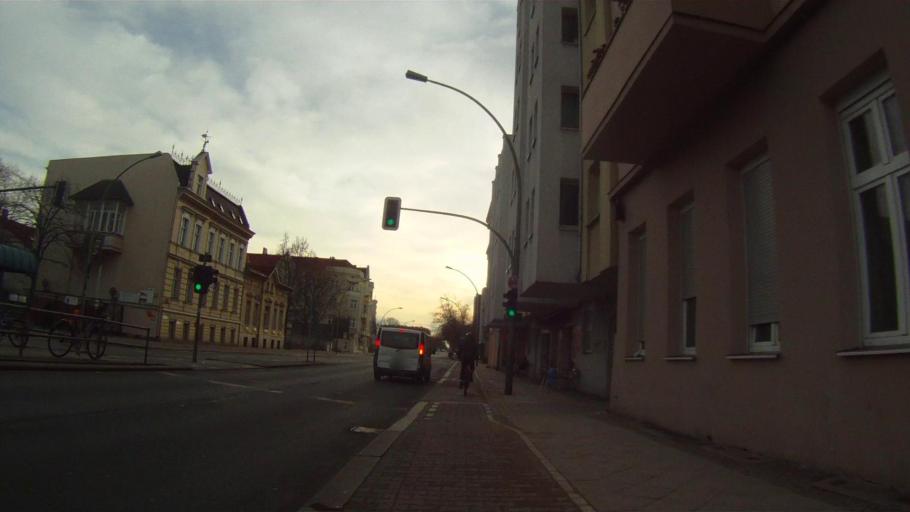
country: DE
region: Berlin
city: Britz
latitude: 52.4623
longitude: 13.4451
